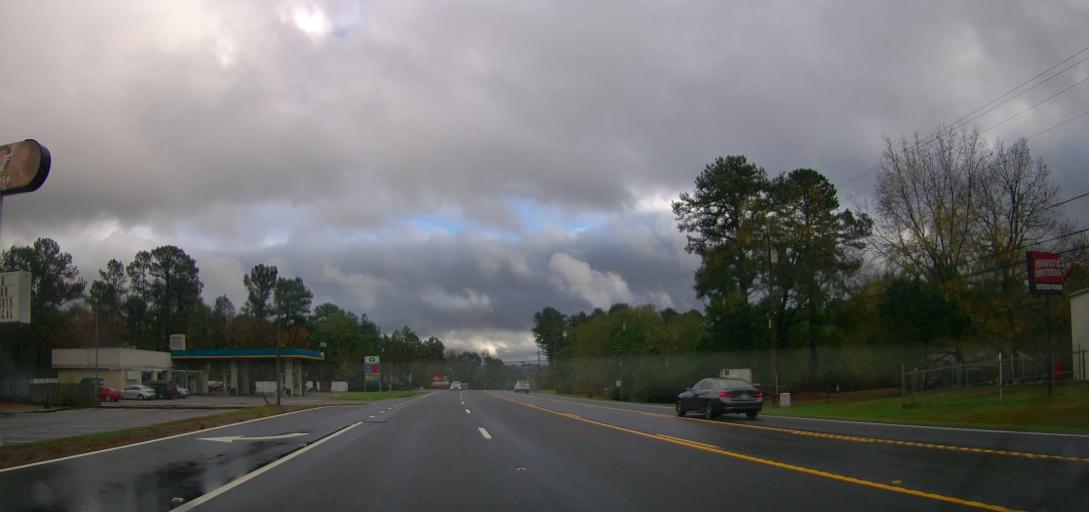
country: US
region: Georgia
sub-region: Clarke County
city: Country Club Estates
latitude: 33.9936
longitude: -83.3797
